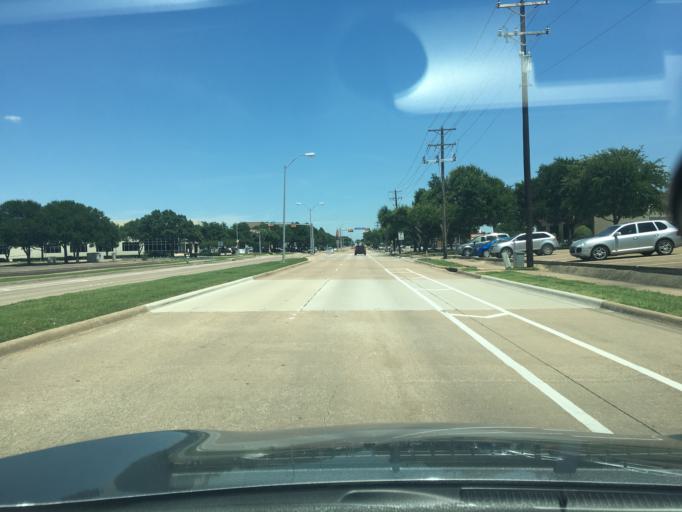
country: US
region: Texas
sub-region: Dallas County
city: Richardson
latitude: 32.9679
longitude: -96.7078
